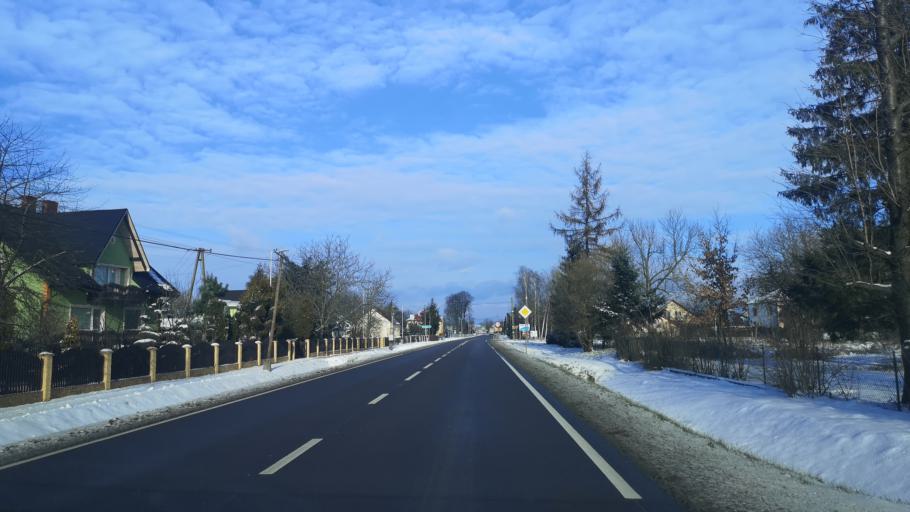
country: PL
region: Subcarpathian Voivodeship
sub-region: Powiat przeworski
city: Tryncza
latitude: 50.1615
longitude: 22.5782
